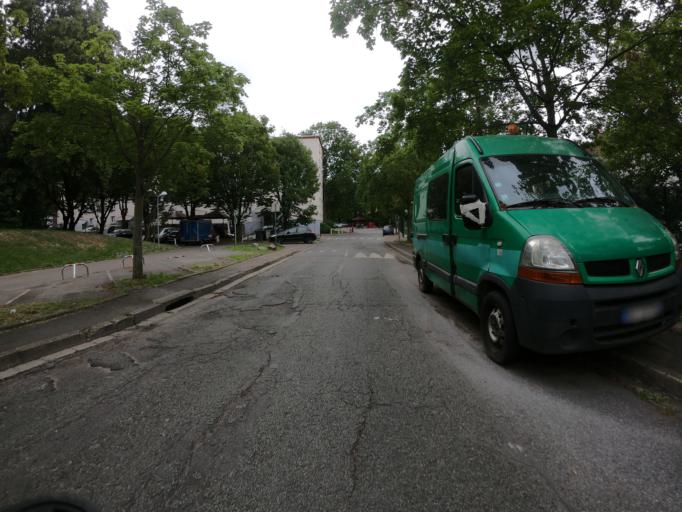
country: FR
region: Ile-de-France
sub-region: Departement du Val-de-Marne
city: Fresnes
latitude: 48.7638
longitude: 2.3245
